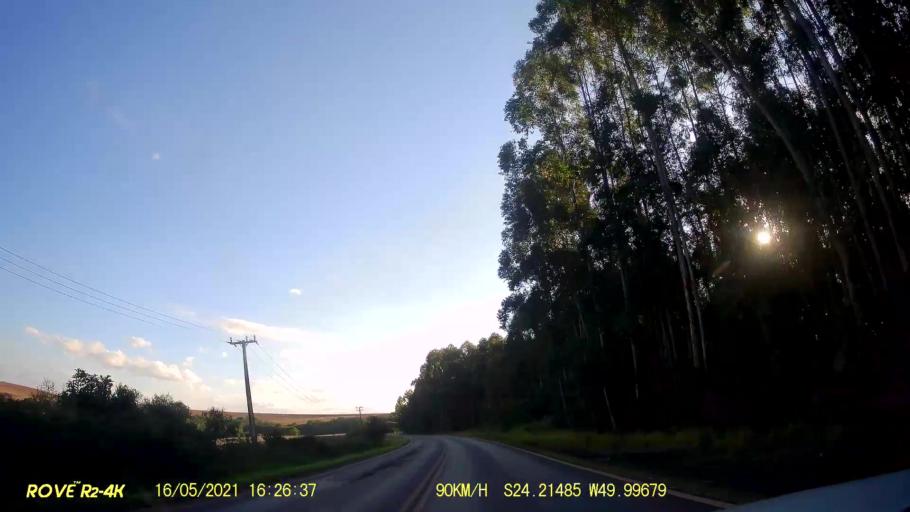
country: BR
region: Parana
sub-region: Jaguariaiva
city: Jaguariaiva
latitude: -24.2148
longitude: -49.9970
